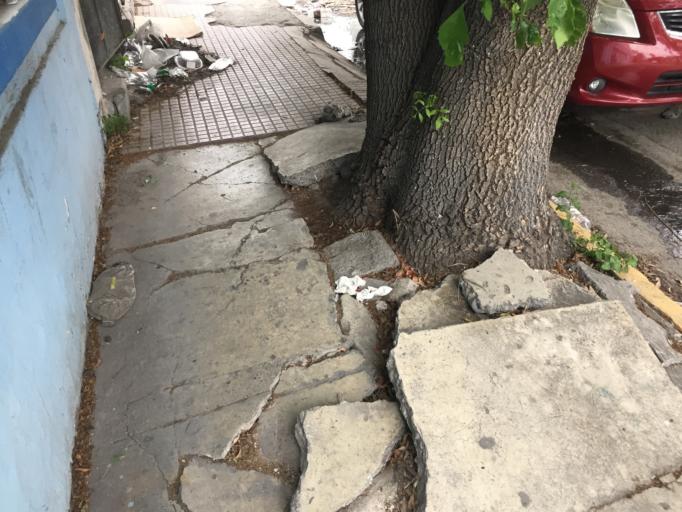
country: MX
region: Nuevo Leon
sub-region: Monterrey
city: Monterrey
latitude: 25.6790
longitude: -100.3063
